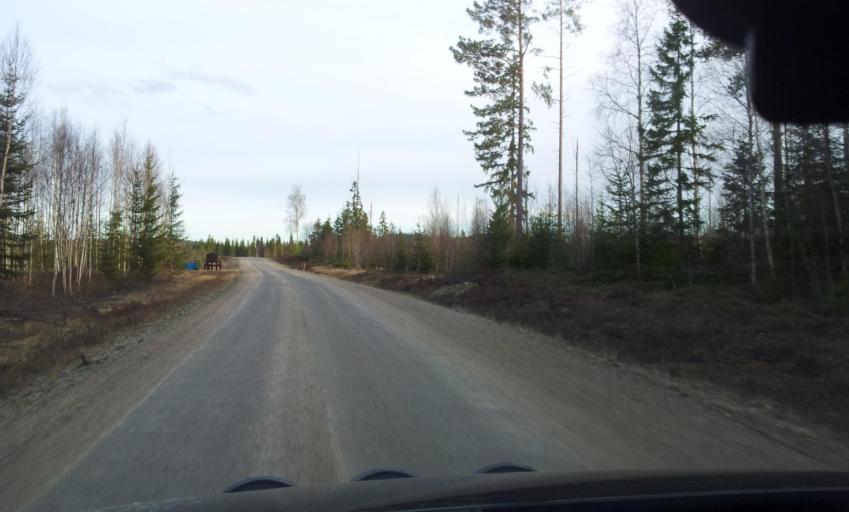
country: SE
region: Gaevleborg
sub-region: Ljusdals Kommun
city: Farila
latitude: 62.1309
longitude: 15.6634
